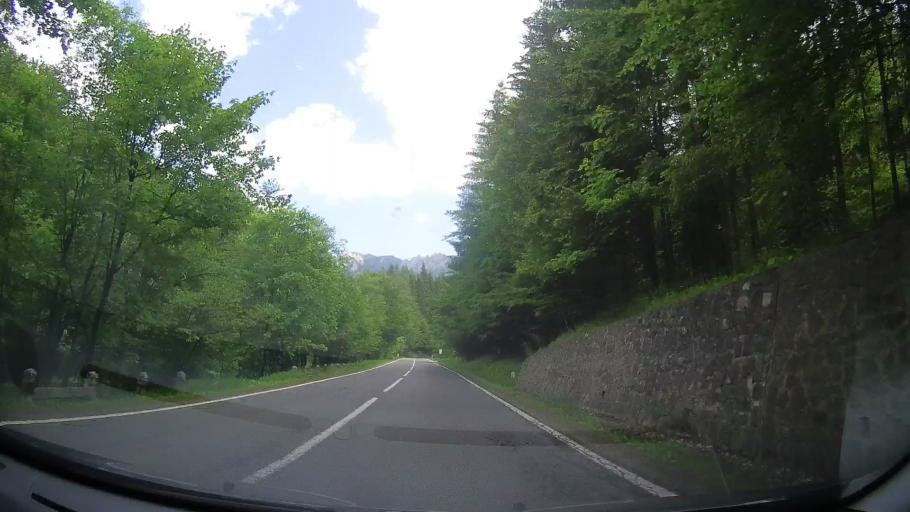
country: RO
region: Brasov
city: Crivina
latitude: 45.4563
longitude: 25.9497
